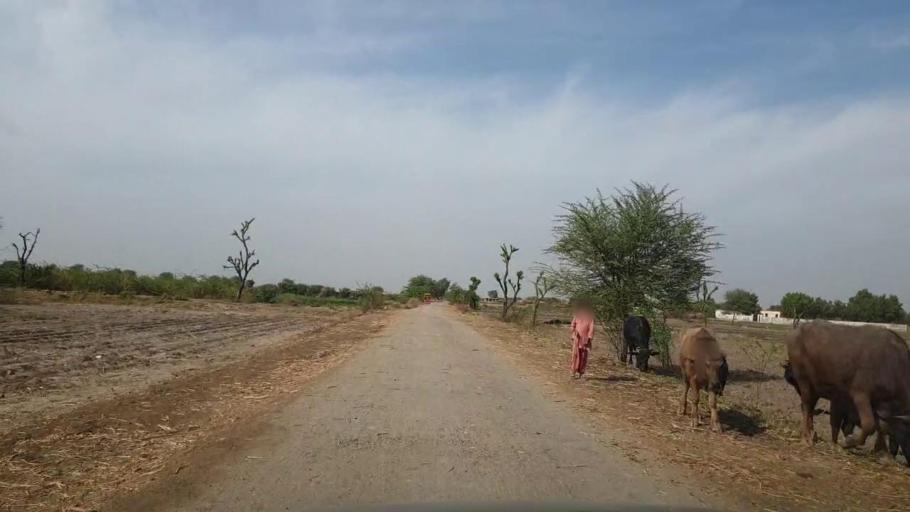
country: PK
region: Sindh
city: Kunri
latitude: 25.1571
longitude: 69.4716
